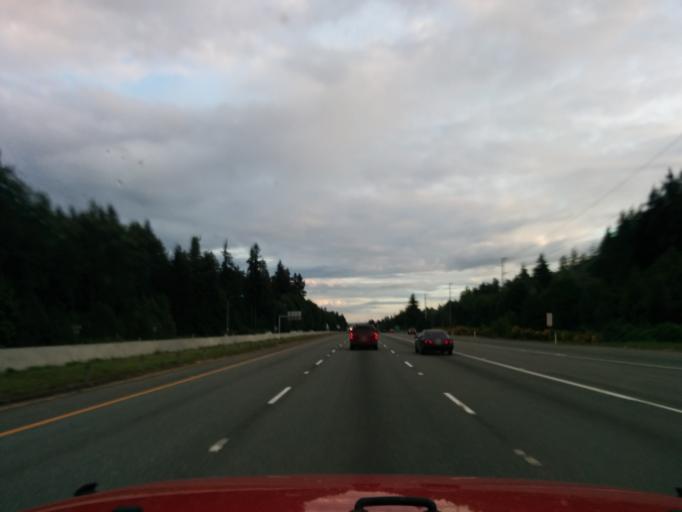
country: US
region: Washington
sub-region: Snohomish County
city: Marysville
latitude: 48.0738
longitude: -122.1850
